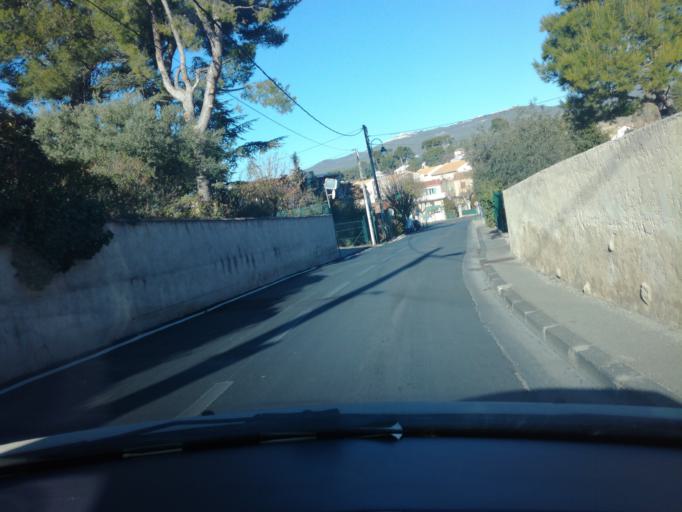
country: FR
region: Provence-Alpes-Cote d'Azur
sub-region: Departement des Bouches-du-Rhone
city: Plan-de-Cuques
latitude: 43.3318
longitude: 5.4645
